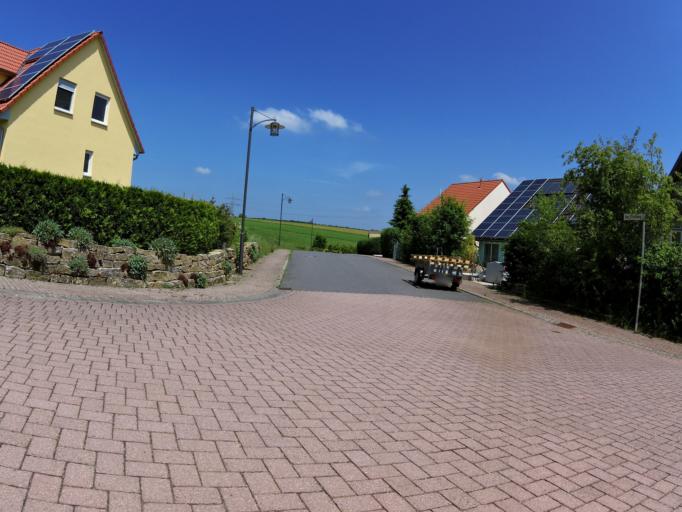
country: DE
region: Bavaria
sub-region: Regierungsbezirk Unterfranken
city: Kleinrinderfeld
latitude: 49.7044
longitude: 9.8452
